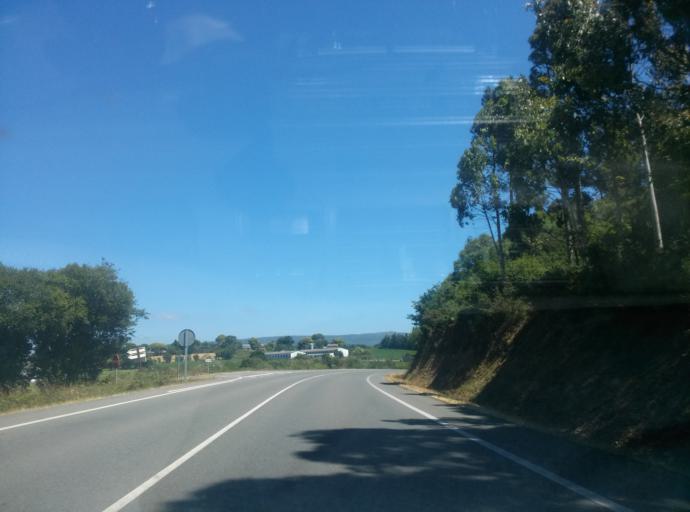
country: ES
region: Galicia
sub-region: Provincia de Lugo
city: Castro de Rei
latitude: 43.2327
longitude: -7.3570
